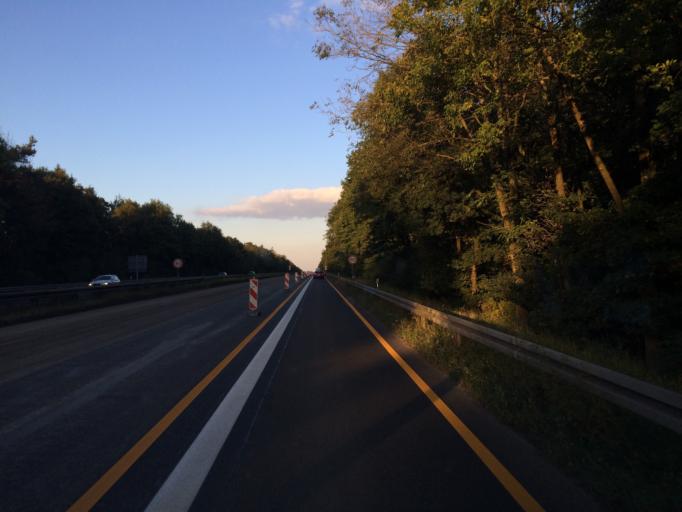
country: DE
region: Rheinland-Pfalz
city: Waldmohr
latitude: 49.3567
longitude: 7.3302
